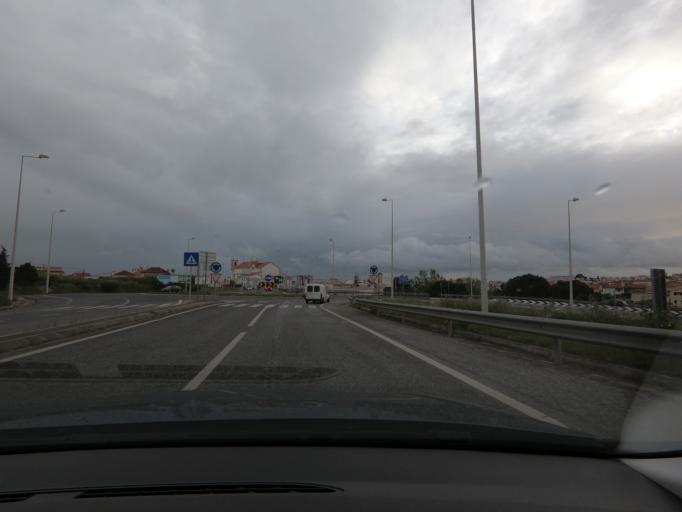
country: PT
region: Lisbon
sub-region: Cascais
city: Sao Domingos de Rana
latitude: 38.7048
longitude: -9.3402
